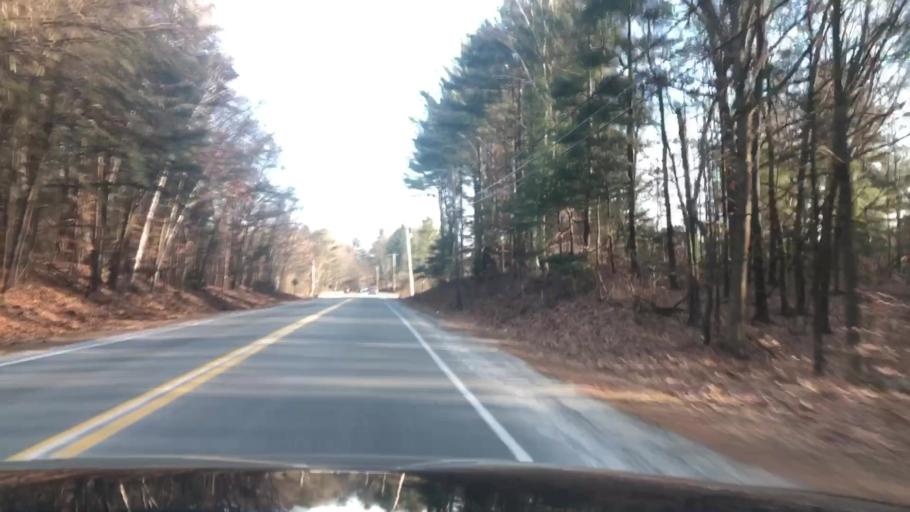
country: US
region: Massachusetts
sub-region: Worcester County
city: Bolton
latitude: 42.4483
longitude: -71.6333
